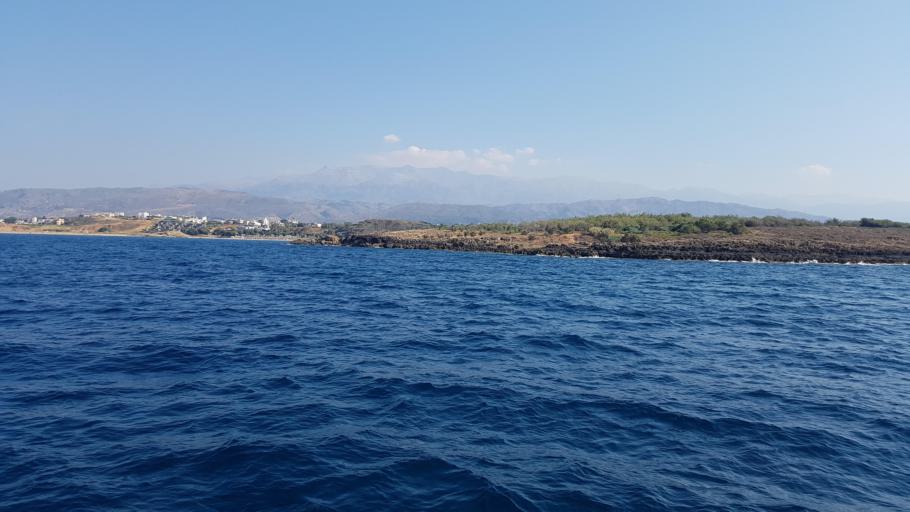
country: GR
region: Crete
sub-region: Nomos Chanias
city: Daratsos
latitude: 35.5203
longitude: 23.9892
